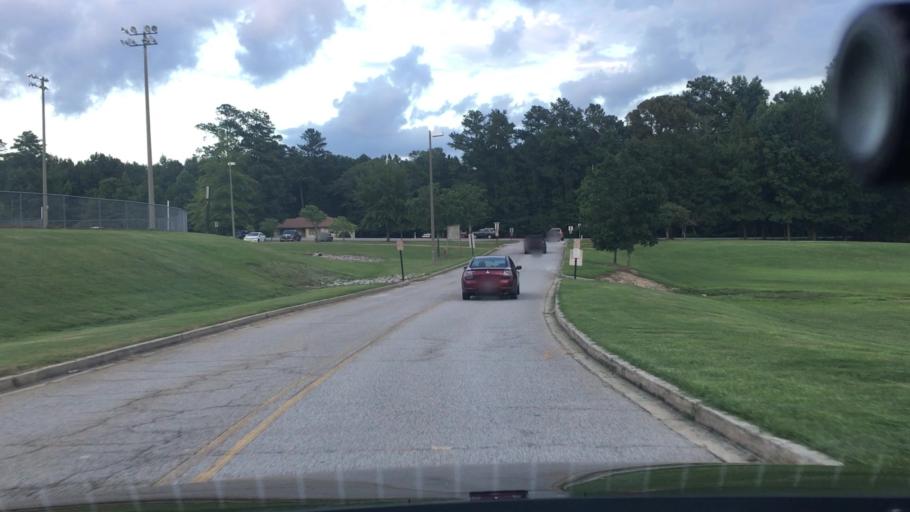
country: US
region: Georgia
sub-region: Coweta County
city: East Newnan
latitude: 33.3365
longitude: -84.6899
